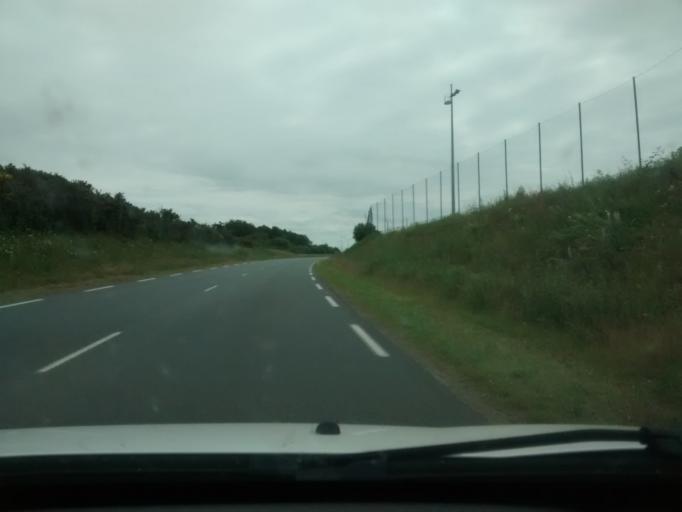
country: FR
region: Brittany
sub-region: Departement des Cotes-d'Armor
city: Saint-Quay-Perros
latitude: 48.7603
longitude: -3.4470
